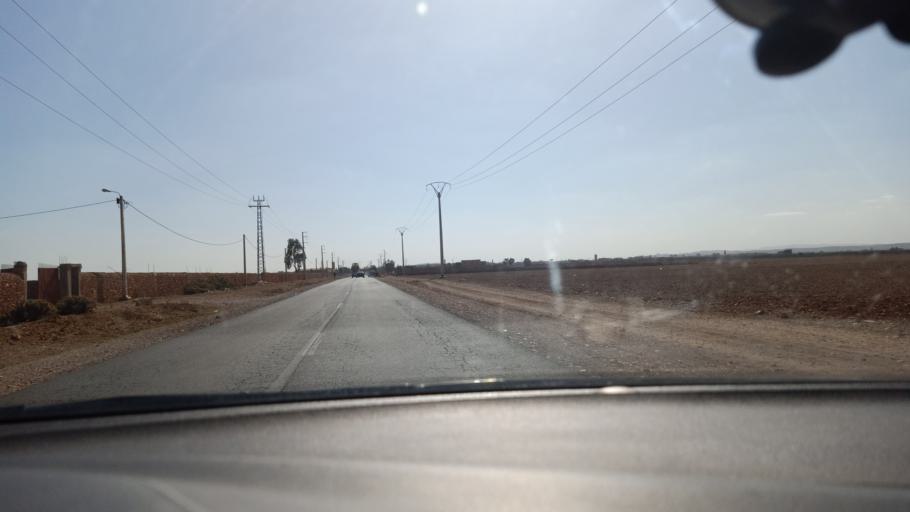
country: MA
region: Doukkala-Abda
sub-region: Safi
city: Youssoufia
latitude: 32.1102
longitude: -8.6086
